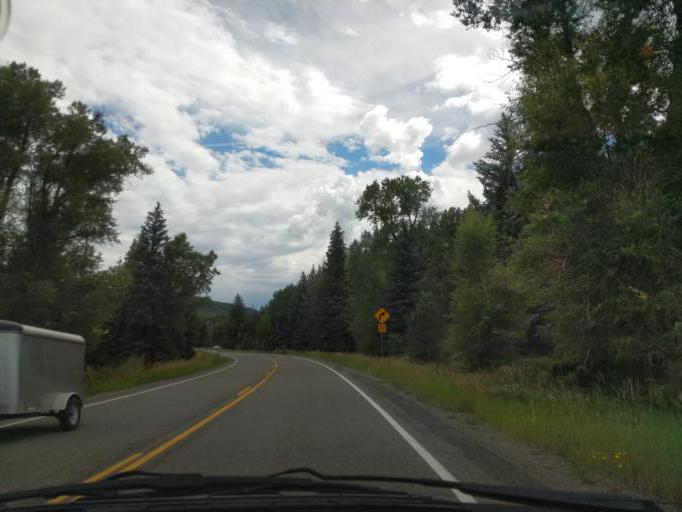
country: US
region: Colorado
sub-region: Delta County
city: Paonia
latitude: 39.0602
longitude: -107.3637
